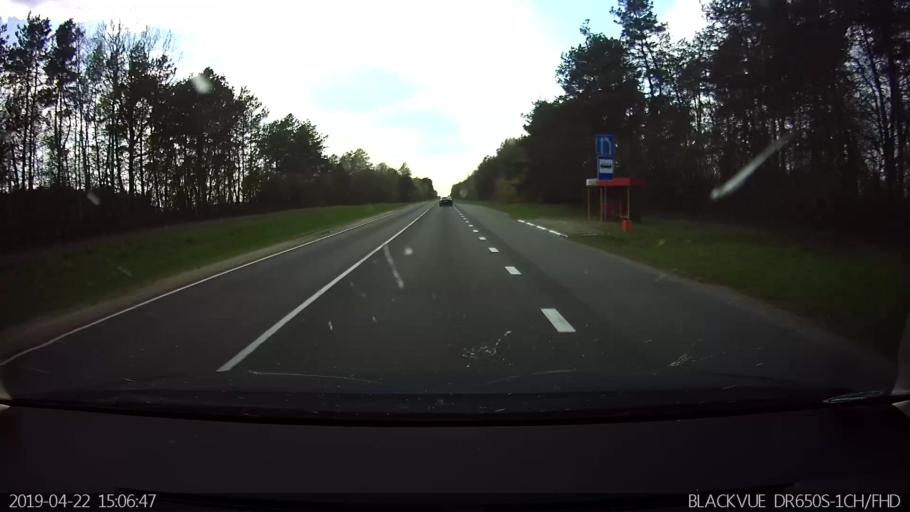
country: BY
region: Brest
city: Kamyanyets
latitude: 52.3307
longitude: 23.8270
